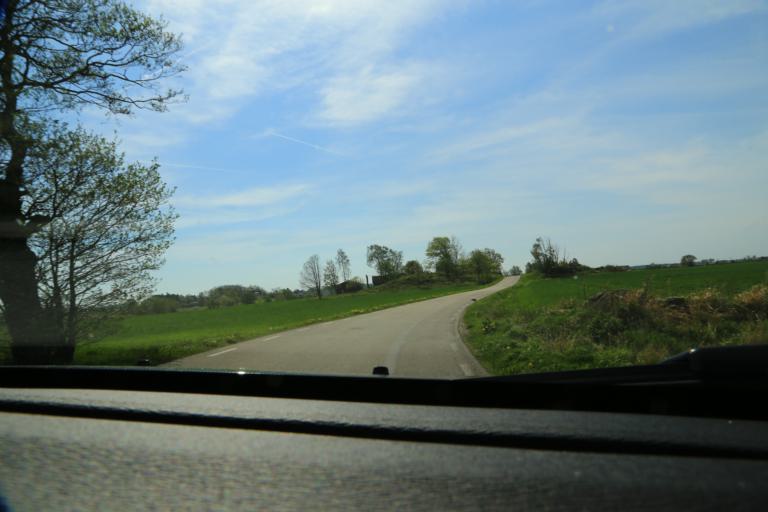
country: SE
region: Halland
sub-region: Varbergs Kommun
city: Traslovslage
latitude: 57.1192
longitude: 12.3493
